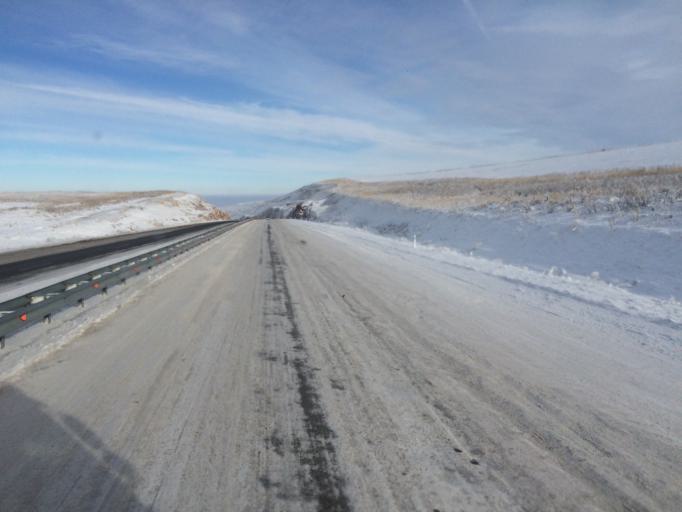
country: KZ
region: Zhambyl
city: Georgiyevka
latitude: 43.4058
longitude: 74.8599
